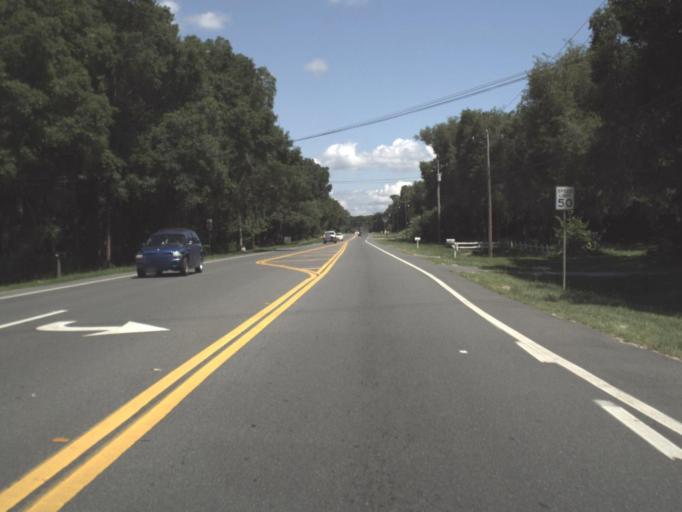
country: US
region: Florida
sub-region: Clay County
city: Keystone Heights
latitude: 29.7718
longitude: -82.0118
